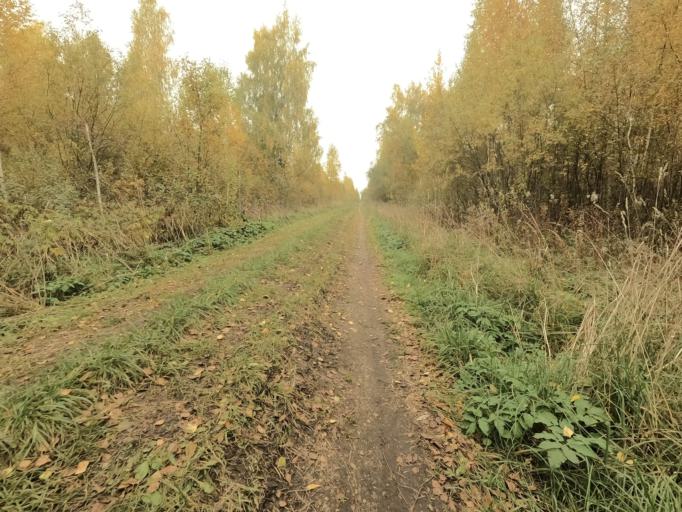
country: RU
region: Novgorod
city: Pankovka
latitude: 58.8836
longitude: 30.9451
